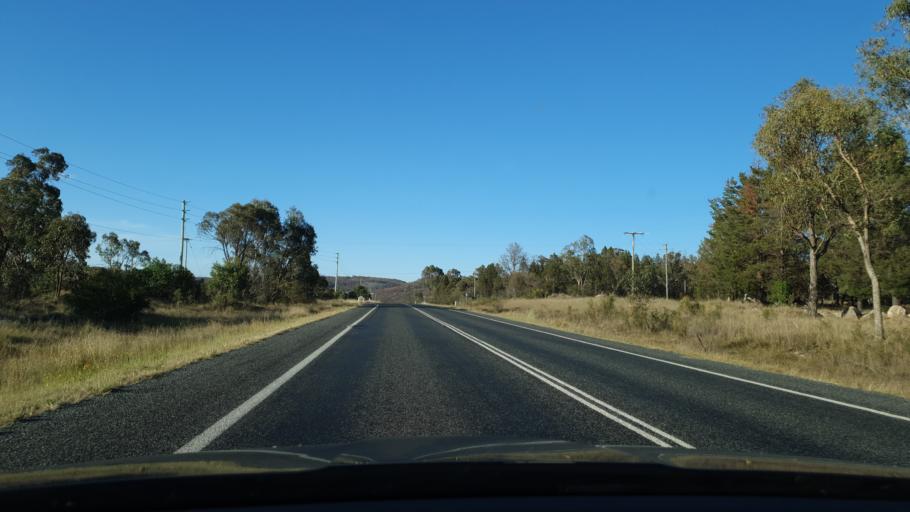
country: AU
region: Queensland
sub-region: Southern Downs
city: Stanthorpe
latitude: -28.6631
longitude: 151.9159
